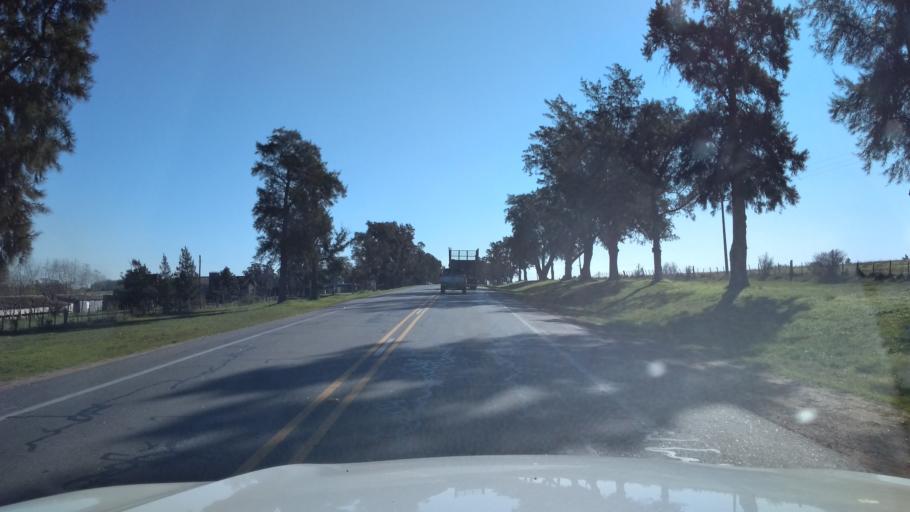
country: UY
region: Canelones
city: San Jacinto
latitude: -34.5439
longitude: -55.8817
